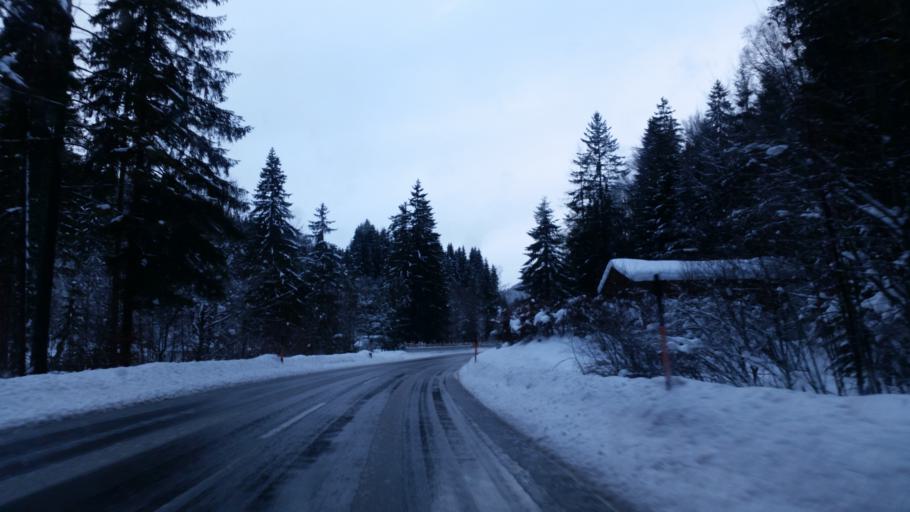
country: AT
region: Salzburg
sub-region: Politischer Bezirk Zell am See
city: Leogang
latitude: 47.4433
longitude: 12.6962
